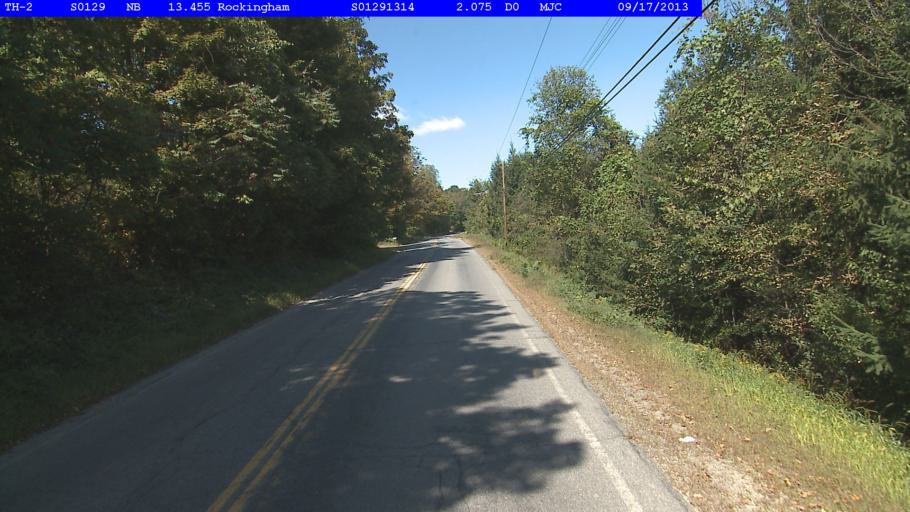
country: US
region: Vermont
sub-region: Windham County
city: Rockingham
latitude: 43.1474
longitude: -72.5186
